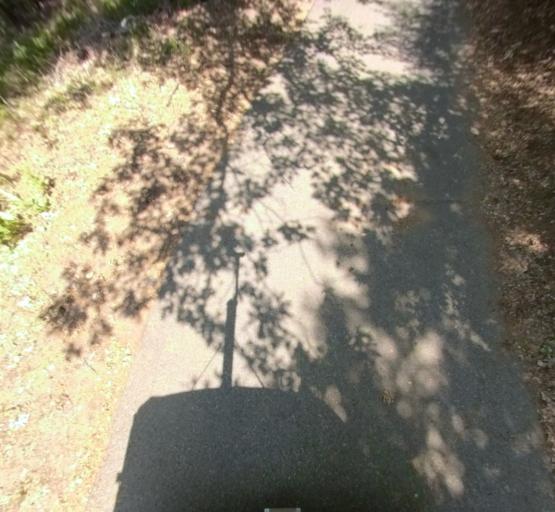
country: US
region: California
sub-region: Fresno County
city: Auberry
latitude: 37.2379
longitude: -119.4542
